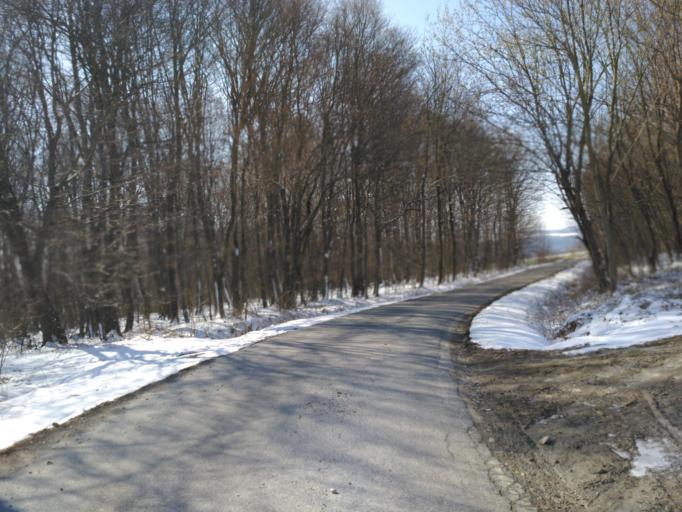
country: PL
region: Subcarpathian Voivodeship
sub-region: Powiat ropczycko-sedziszowski
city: Wielopole Skrzynskie
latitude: 49.9736
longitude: 21.6048
